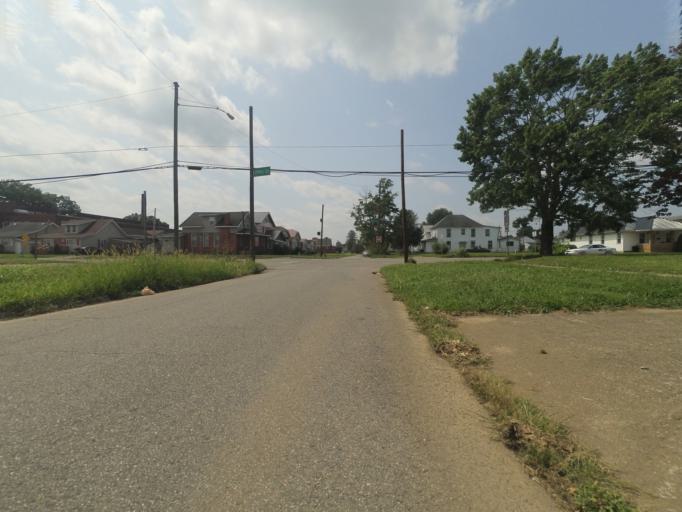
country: US
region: West Virginia
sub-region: Cabell County
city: Huntington
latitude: 38.4285
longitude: -82.3987
